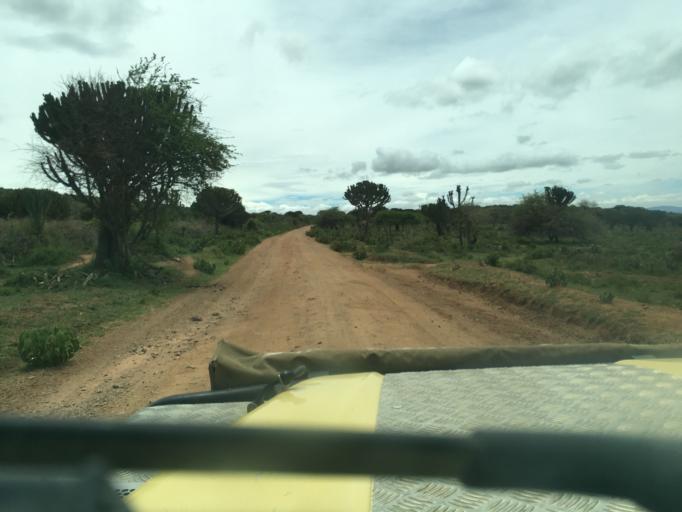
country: KE
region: Kajiado
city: Magadi
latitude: -2.0070
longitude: 35.5241
